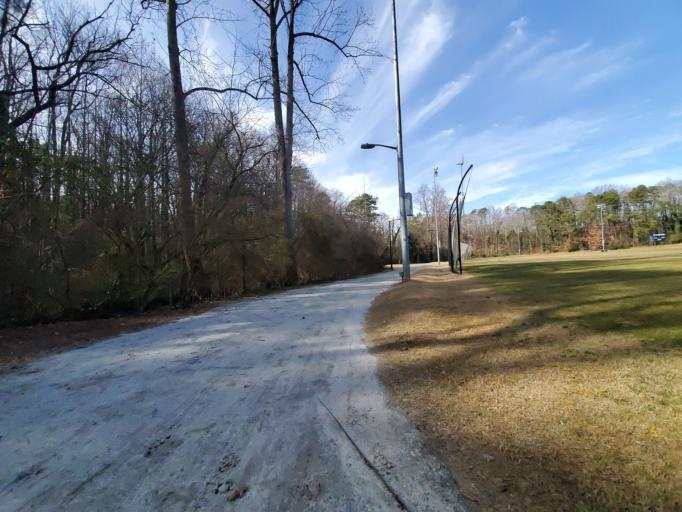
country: US
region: Georgia
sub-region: DeKalb County
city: Druid Hills
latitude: 33.7997
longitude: -84.3330
